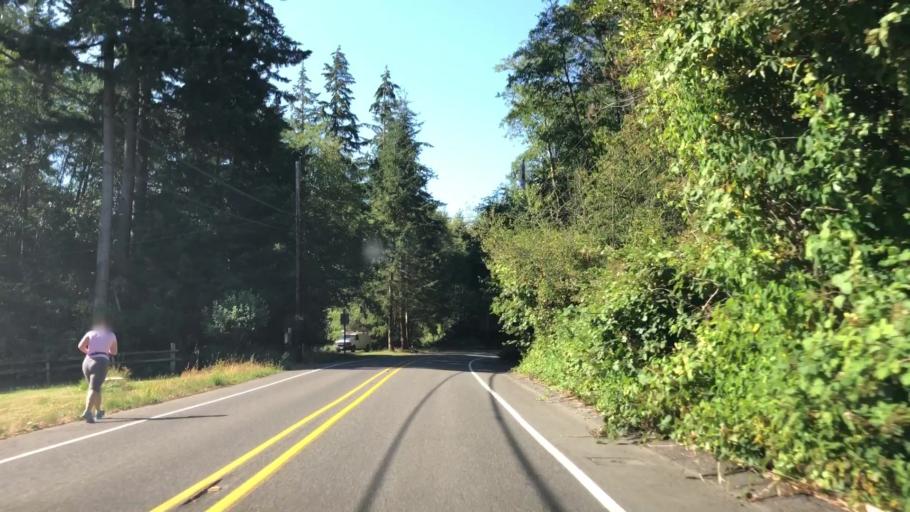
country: US
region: Washington
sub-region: Kitsap County
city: Kingston
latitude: 47.7752
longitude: -122.5021
